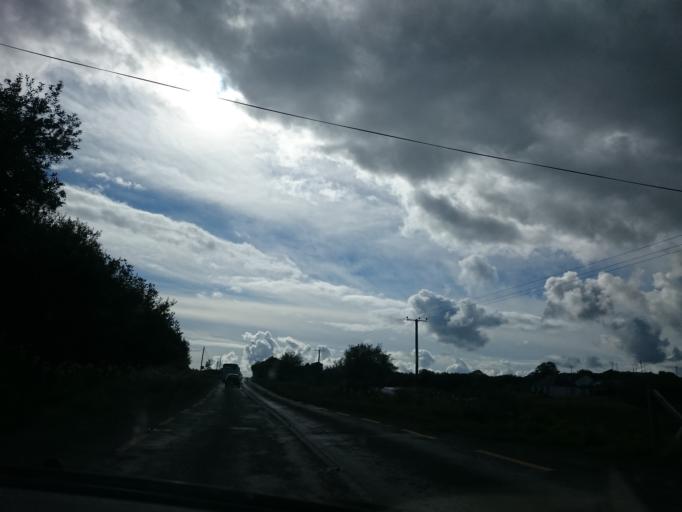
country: IE
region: Connaught
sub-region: Maigh Eo
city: Westport
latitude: 53.9027
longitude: -9.5853
